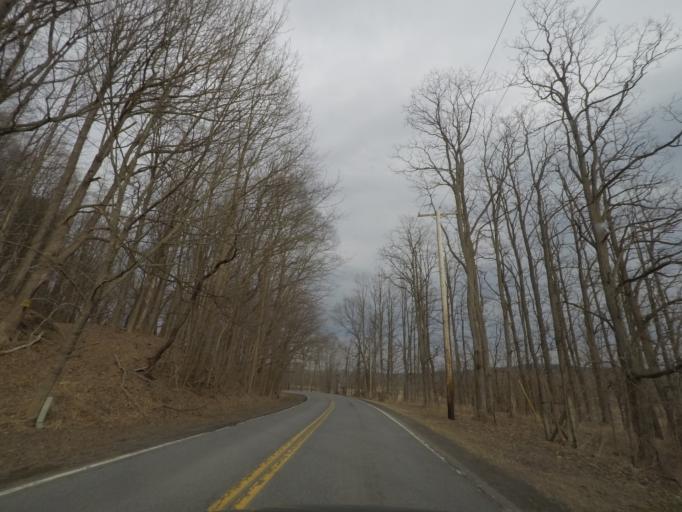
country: US
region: New York
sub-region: Washington County
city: Cambridge
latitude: 42.9569
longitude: -73.4481
